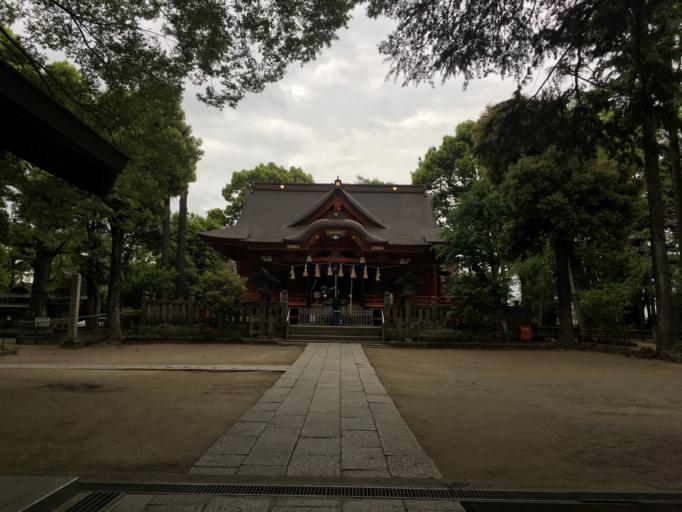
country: JP
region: Chiba
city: Ichihara
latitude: 35.5377
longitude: 140.1173
